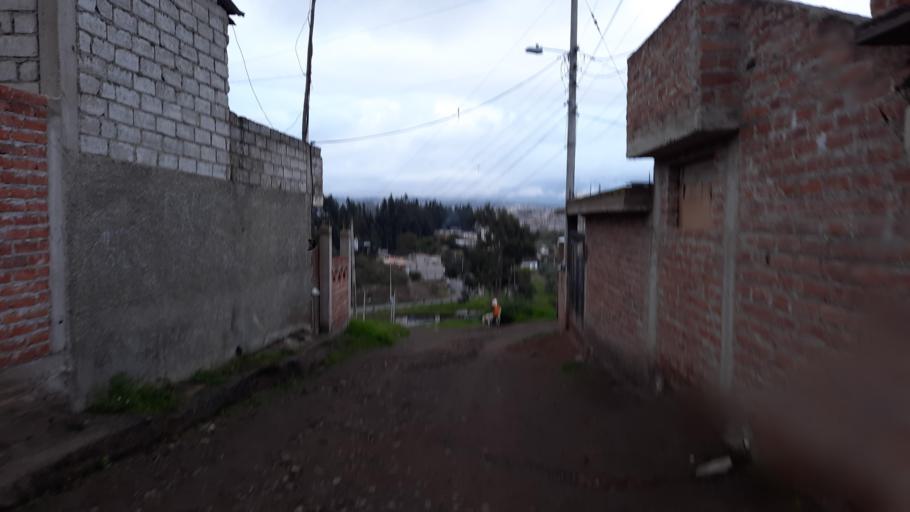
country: EC
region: Chimborazo
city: Riobamba
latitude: -1.6849
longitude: -78.6622
